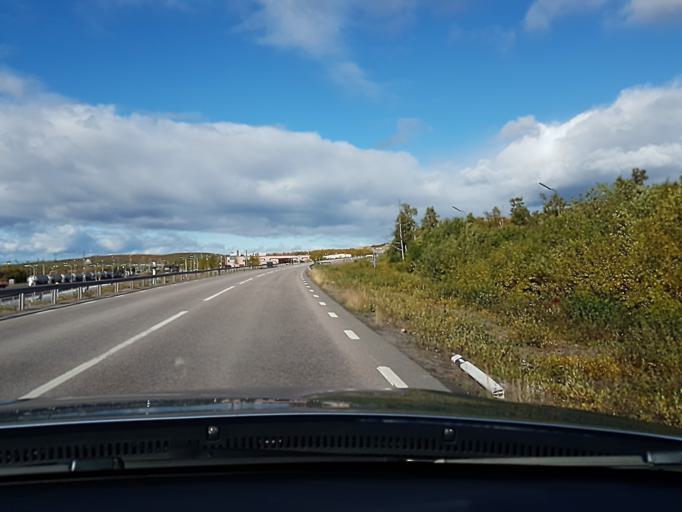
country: SE
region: Norrbotten
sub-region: Kiruna Kommun
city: Kiruna
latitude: 67.8654
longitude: 20.2030
